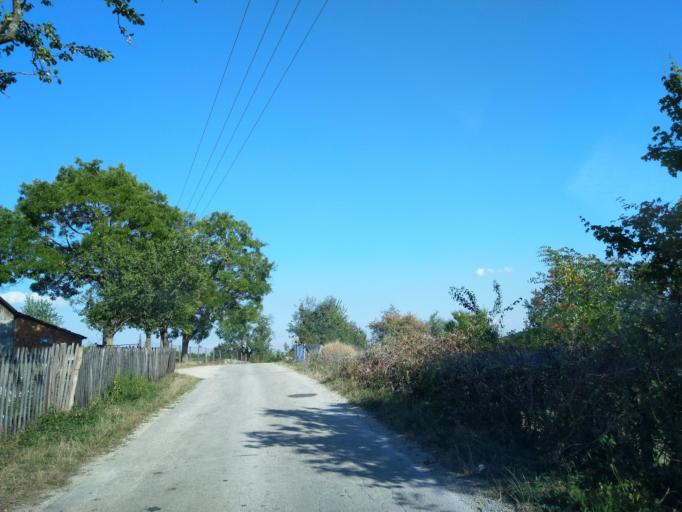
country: RS
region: Central Serbia
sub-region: Zlatiborski Okrug
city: Uzice
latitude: 43.8132
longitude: 19.8537
